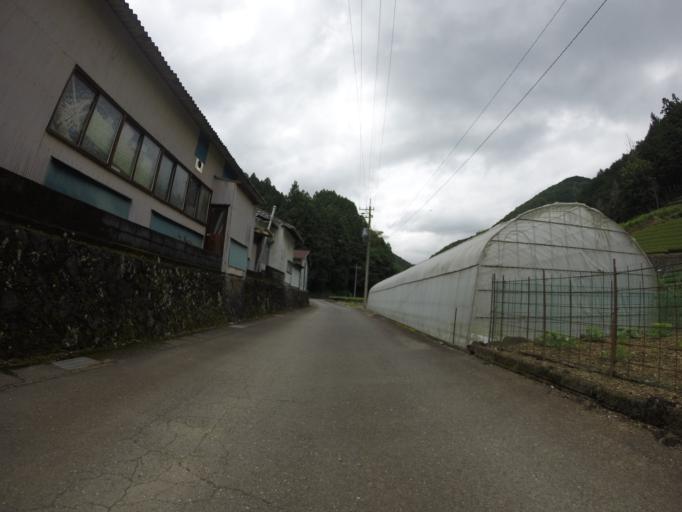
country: JP
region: Shizuoka
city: Shizuoka-shi
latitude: 35.0161
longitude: 138.3073
